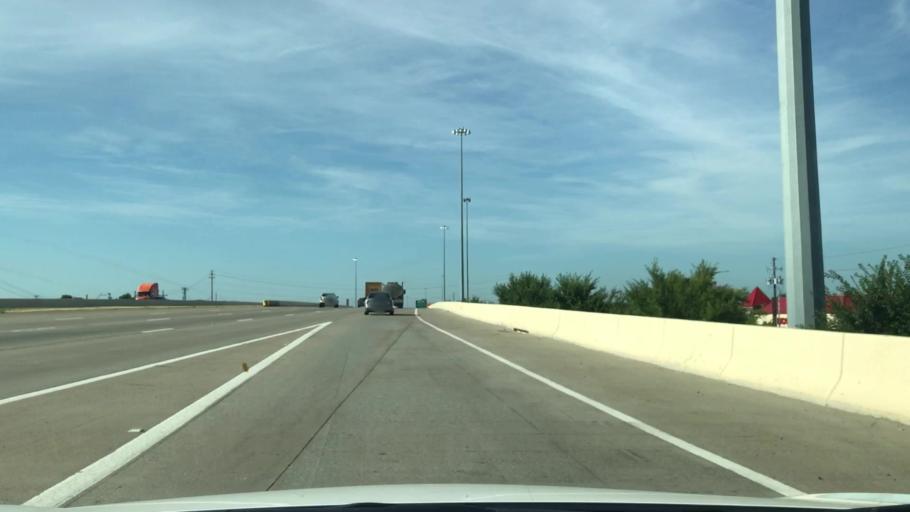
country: US
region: Texas
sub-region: Collin County
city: McKinney
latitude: 33.2189
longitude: -96.6360
